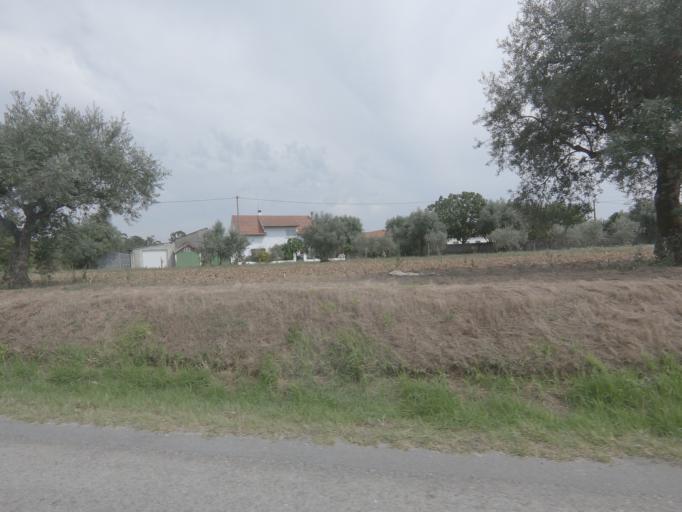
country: PT
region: Leiria
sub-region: Pombal
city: Pombal
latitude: 39.8807
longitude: -8.6774
